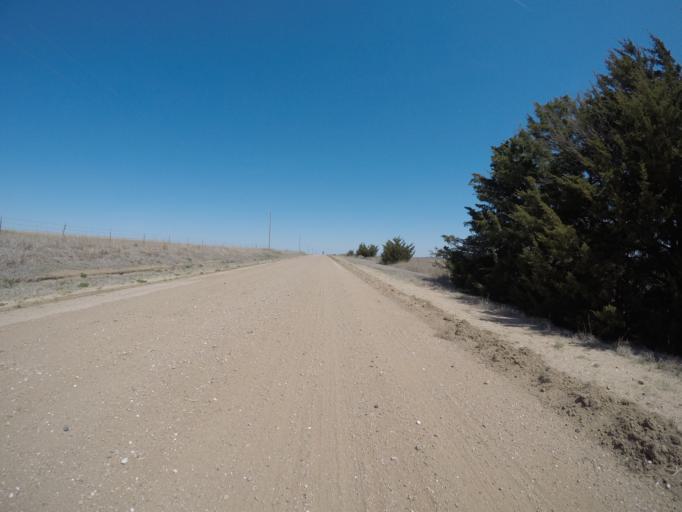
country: US
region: Kansas
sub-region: Pratt County
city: Pratt
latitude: 37.4224
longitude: -98.8388
